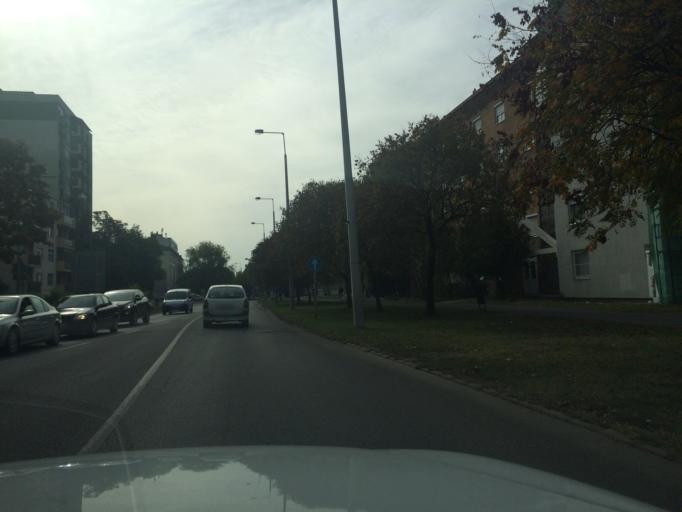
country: HU
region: Szabolcs-Szatmar-Bereg
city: Nyiregyhaza
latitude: 47.9654
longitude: 21.7146
